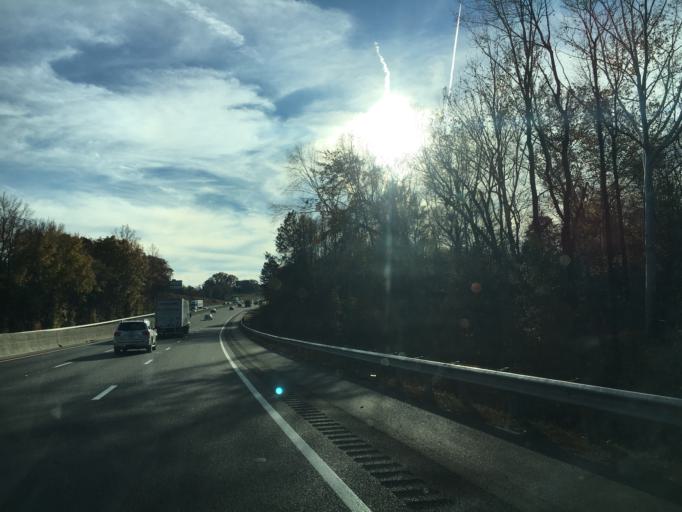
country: US
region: South Carolina
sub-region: Spartanburg County
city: Wellford
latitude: 34.9360
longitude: -82.0774
